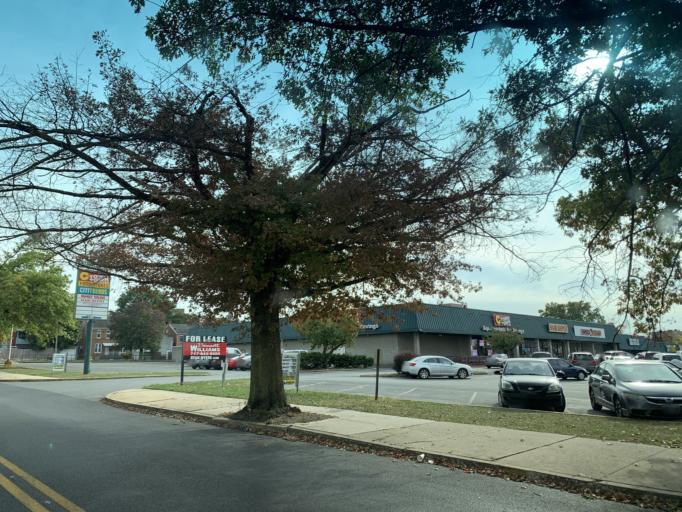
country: US
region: Pennsylvania
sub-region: York County
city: York
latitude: 39.9668
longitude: -76.7254
